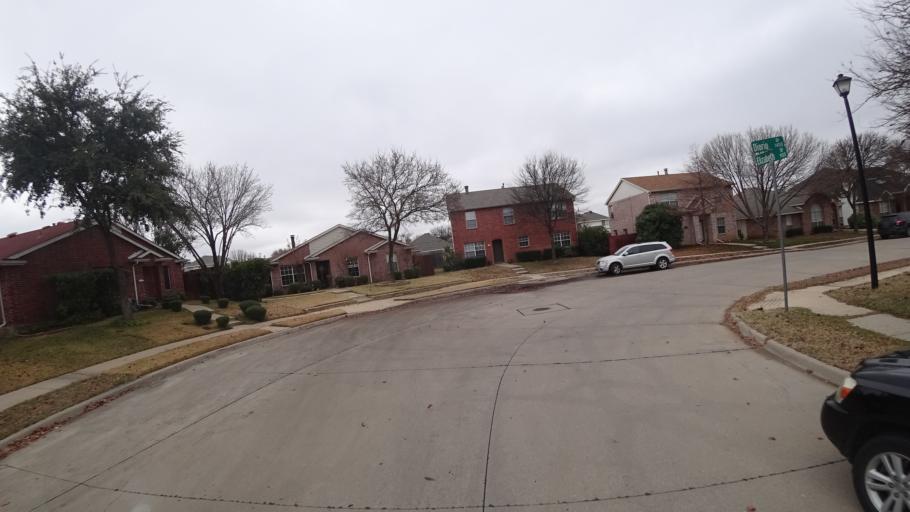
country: US
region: Texas
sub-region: Denton County
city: Lewisville
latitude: 33.0352
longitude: -97.0333
